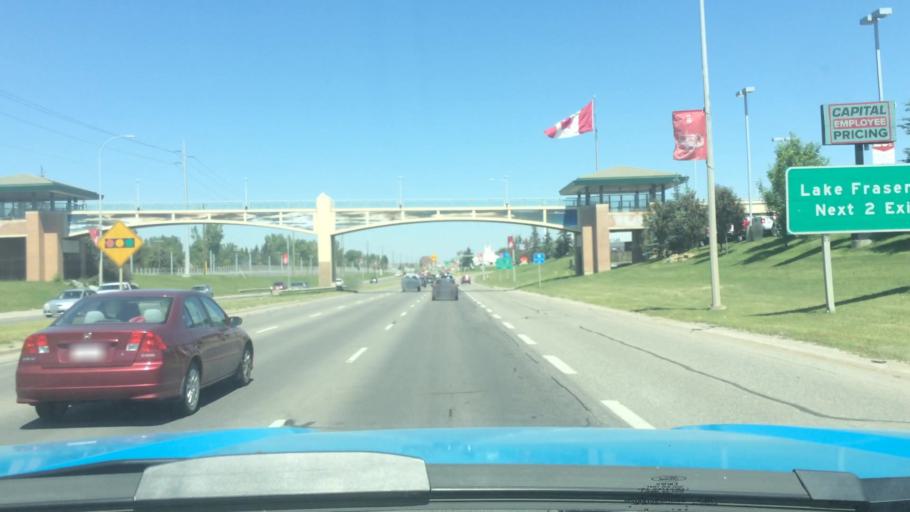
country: CA
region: Alberta
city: Calgary
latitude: 50.9358
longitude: -114.0685
